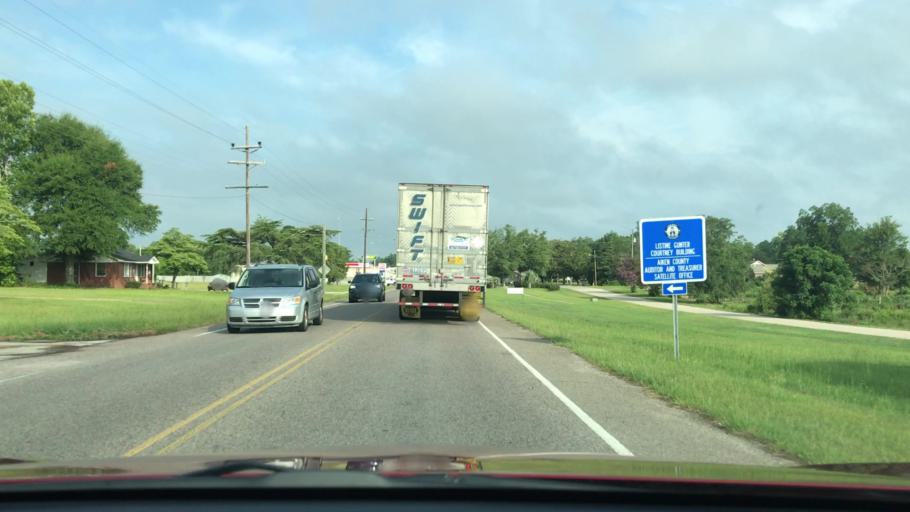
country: US
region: South Carolina
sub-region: Barnwell County
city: Williston
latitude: 33.6489
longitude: -81.3566
